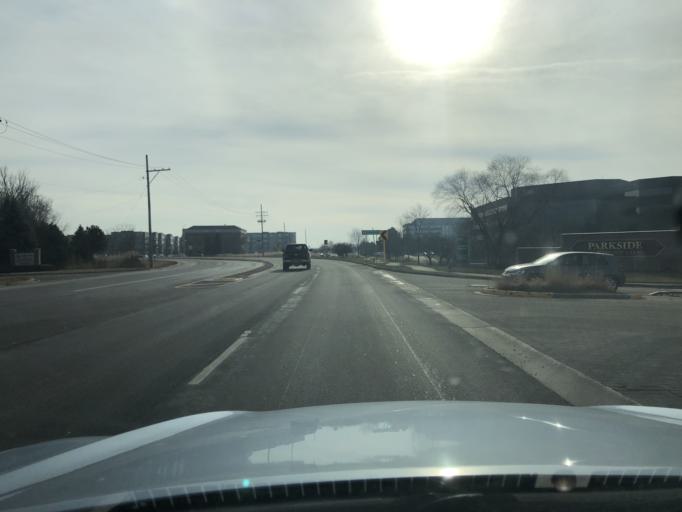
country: US
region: Illinois
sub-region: DuPage County
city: Itasca
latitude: 41.9902
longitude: -88.0033
